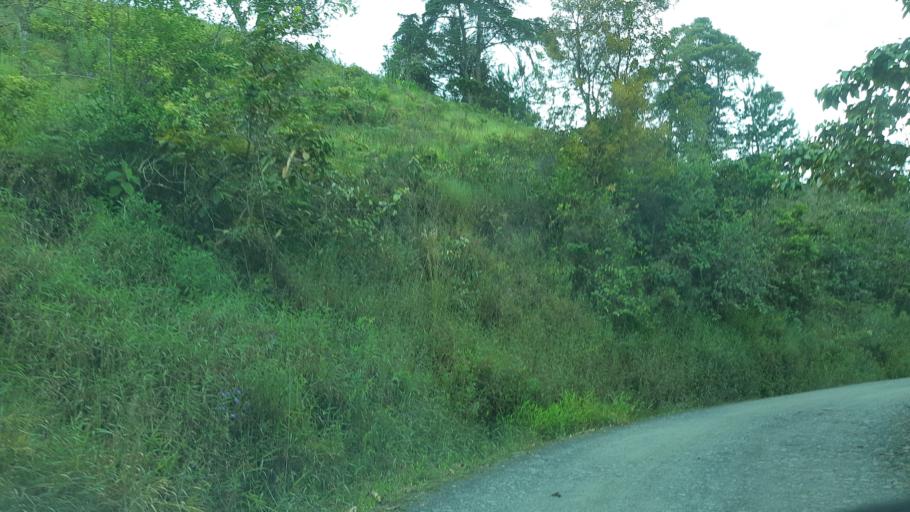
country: CO
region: Boyaca
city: Chivor
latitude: 4.9815
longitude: -73.3225
